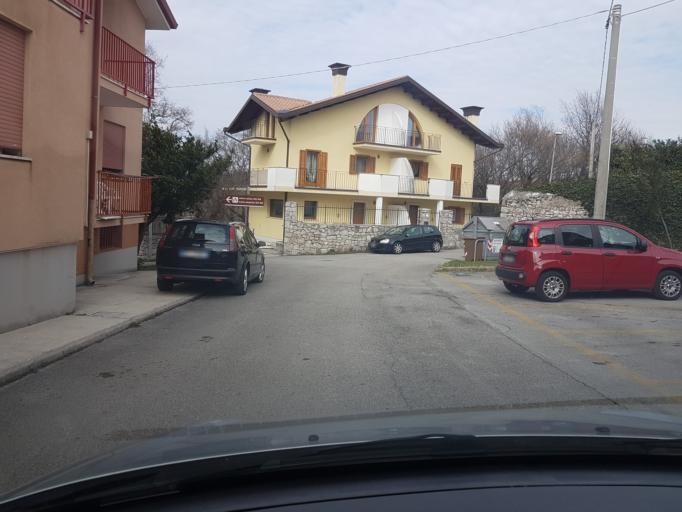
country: IT
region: Friuli Venezia Giulia
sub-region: Provincia di Trieste
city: Aurisina
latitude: 45.7506
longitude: 13.6838
